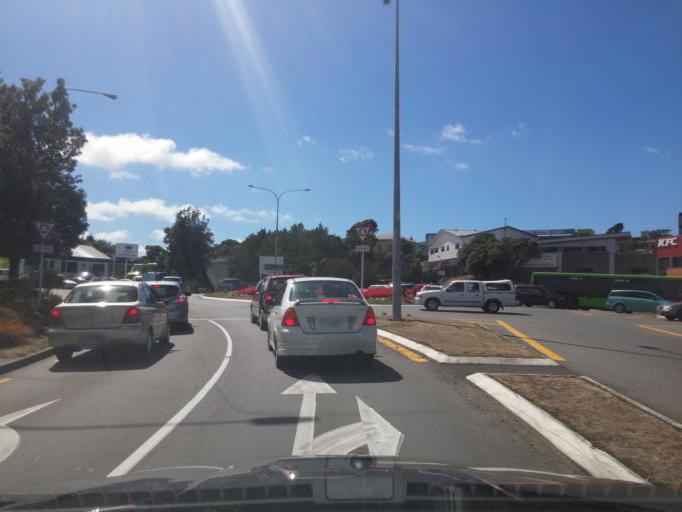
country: NZ
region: Wellington
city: Petone
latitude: -41.2217
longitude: 174.8070
